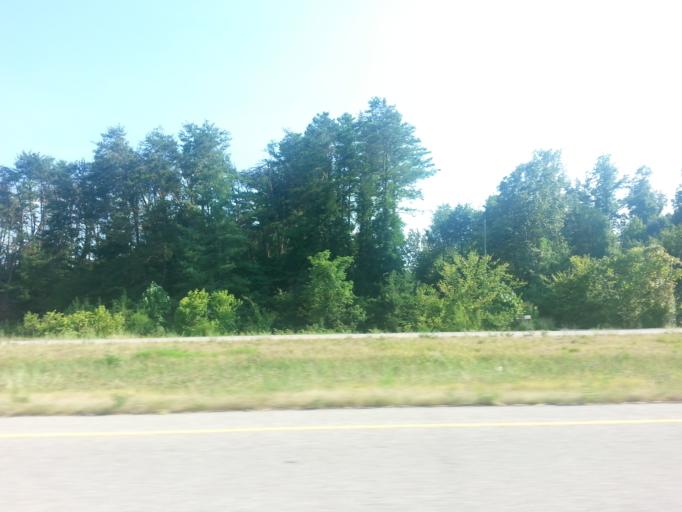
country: US
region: Tennessee
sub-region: Loudon County
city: Greenback
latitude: 35.7379
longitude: -84.1913
